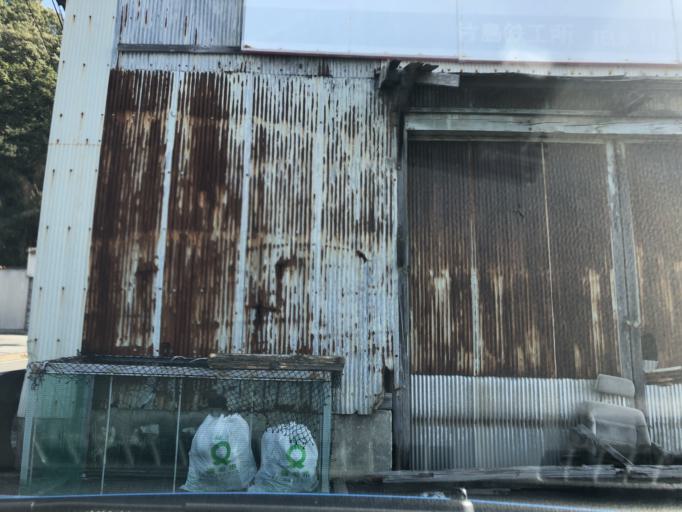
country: JP
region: Kochi
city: Sukumo
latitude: 32.9221
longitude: 132.6947
